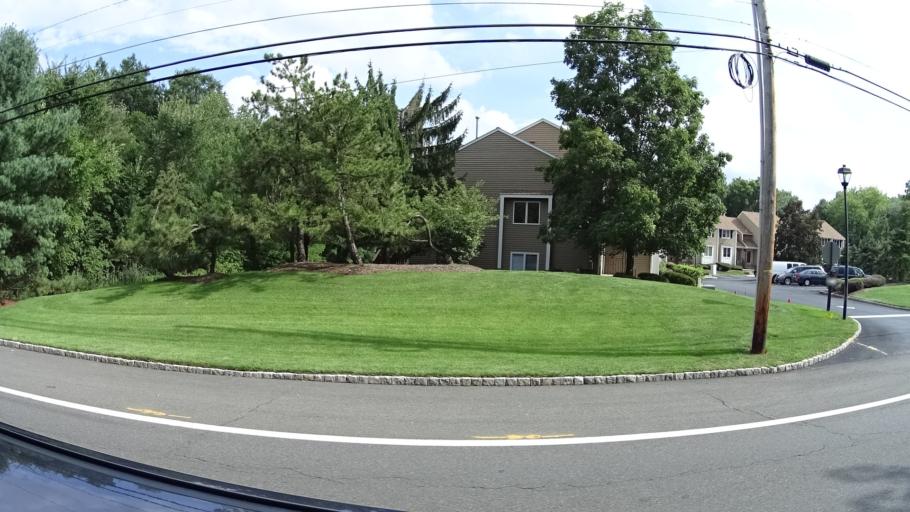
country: US
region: New Jersey
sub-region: Union County
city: Berkeley Heights
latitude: 40.6785
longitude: -74.4548
